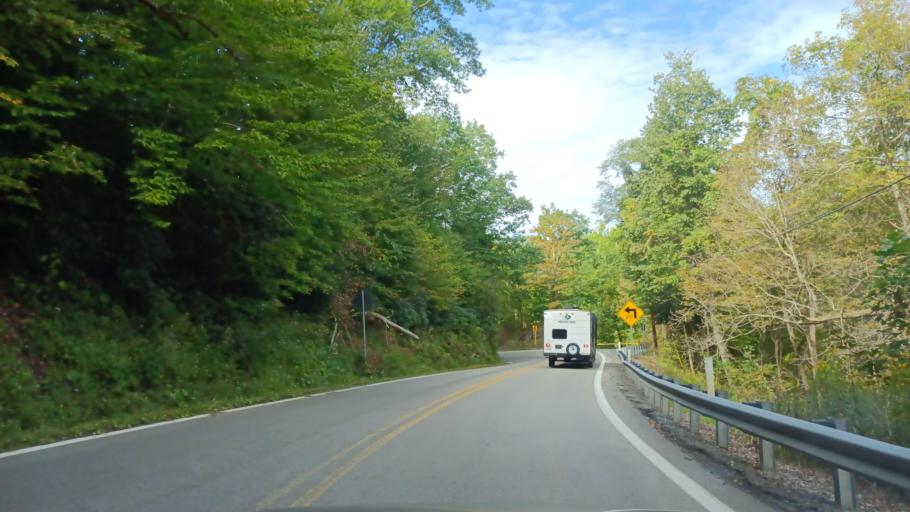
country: US
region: West Virginia
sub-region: Preston County
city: Terra Alta
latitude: 39.3002
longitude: -79.6127
